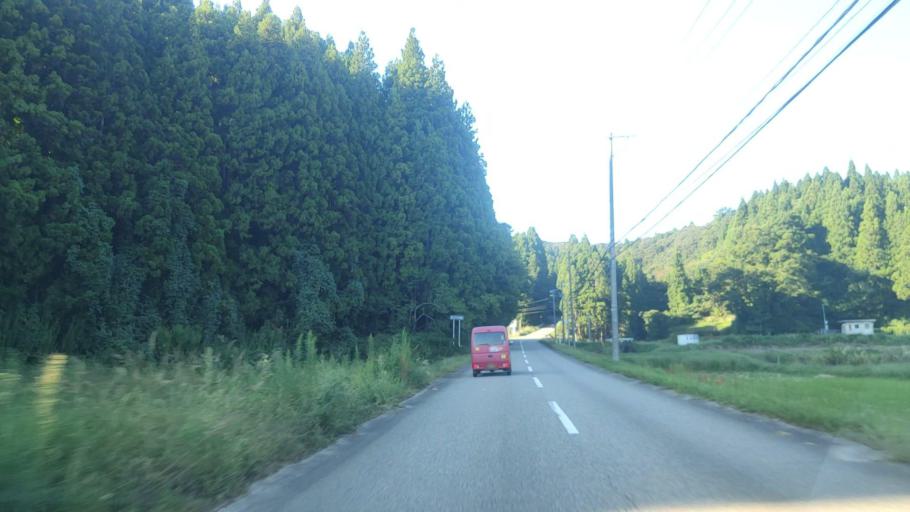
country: JP
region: Ishikawa
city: Nanao
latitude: 37.1080
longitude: 136.9619
